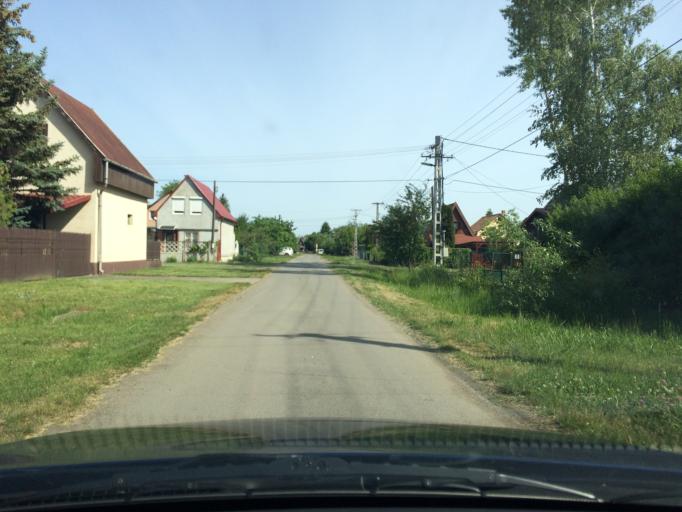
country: HU
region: Szabolcs-Szatmar-Bereg
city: Tiszavasvari
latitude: 47.9525
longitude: 21.3494
